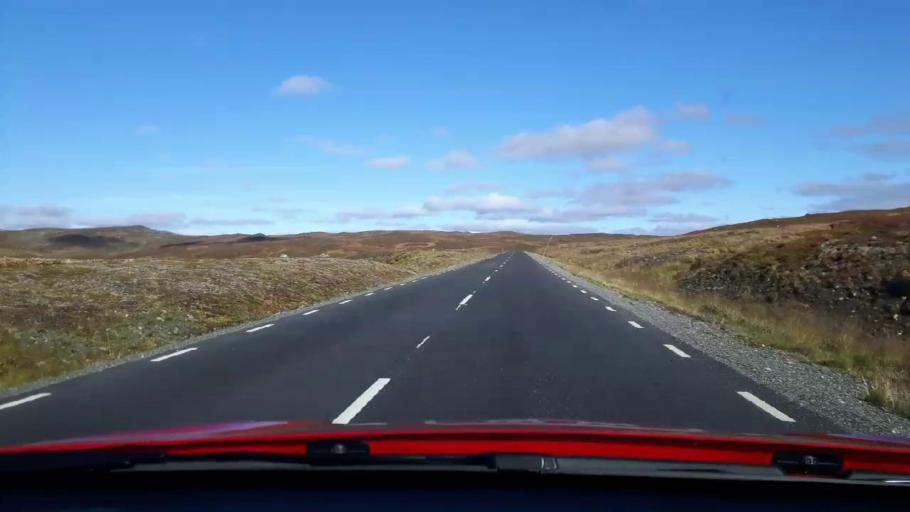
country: NO
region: Nordland
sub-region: Hattfjelldal
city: Hattfjelldal
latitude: 65.0413
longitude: 14.3287
